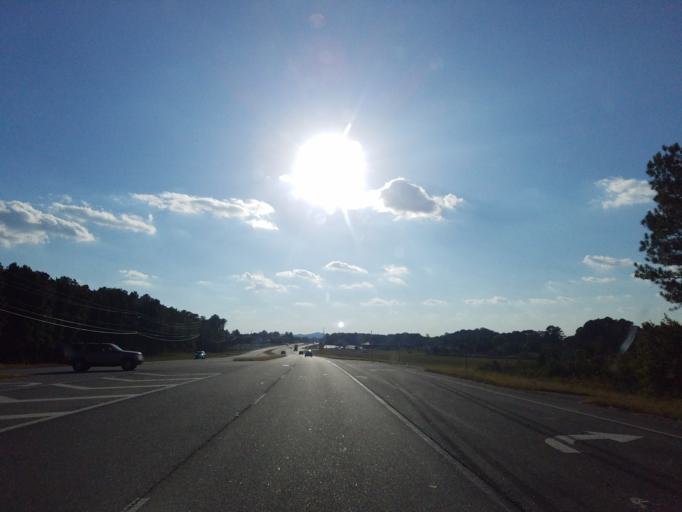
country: US
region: Georgia
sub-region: Bartow County
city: Euharlee
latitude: 34.1034
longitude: -84.9222
